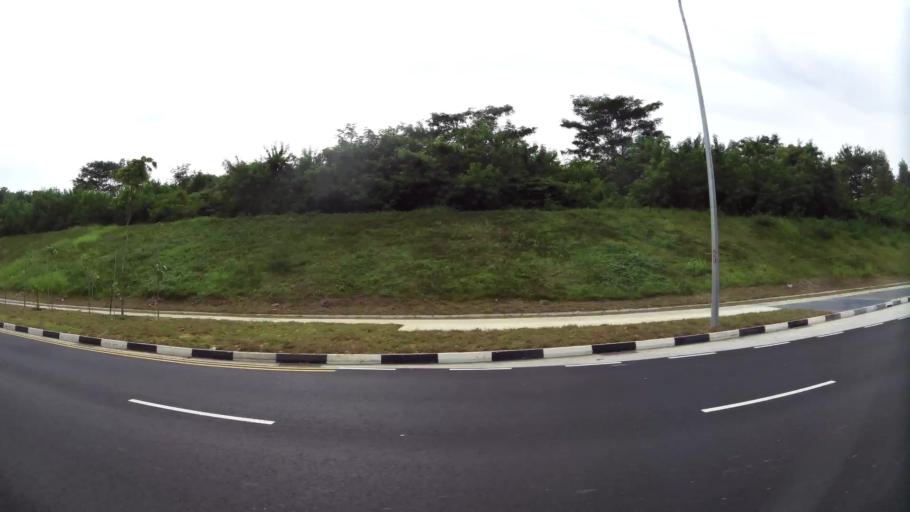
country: MY
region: Johor
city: Johor Bahru
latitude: 1.4274
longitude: 103.7564
